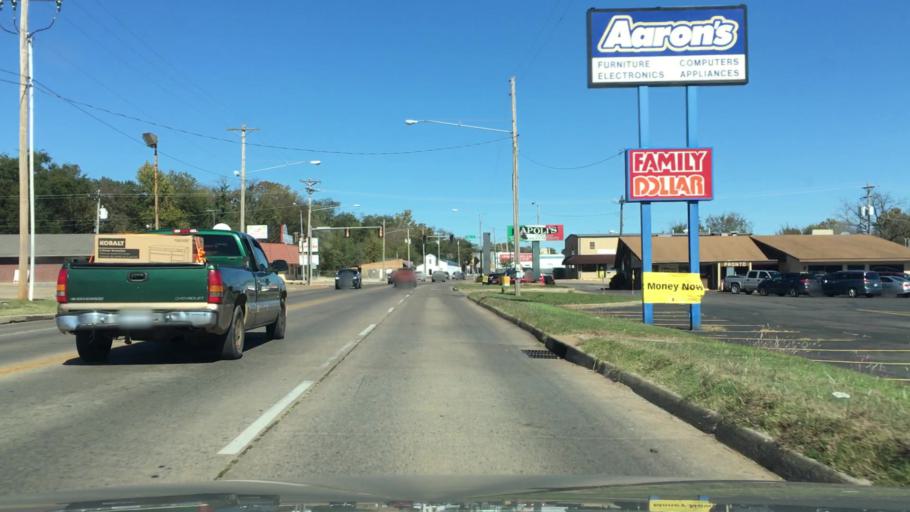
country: US
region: Oklahoma
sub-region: Cherokee County
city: Tahlequah
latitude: 35.9031
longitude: -94.9744
